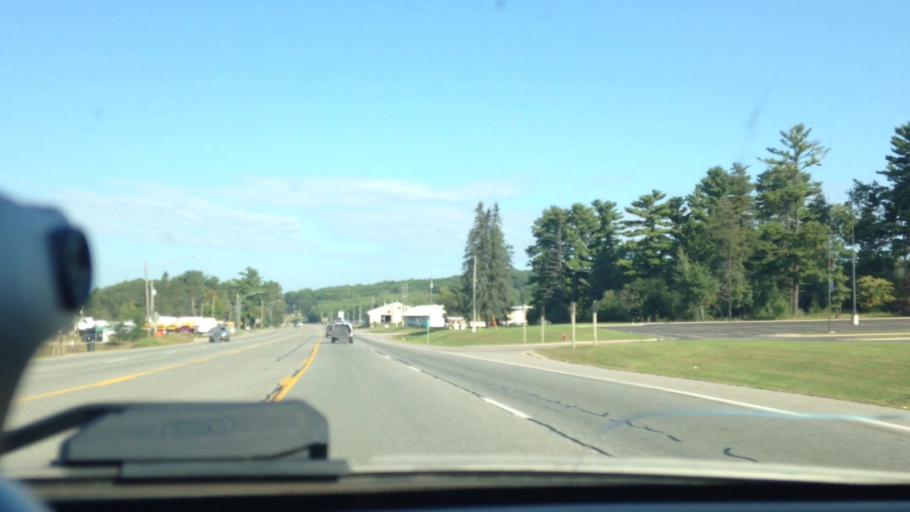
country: US
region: Michigan
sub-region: Dickinson County
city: Iron Mountain
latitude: 45.8467
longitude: -88.0500
